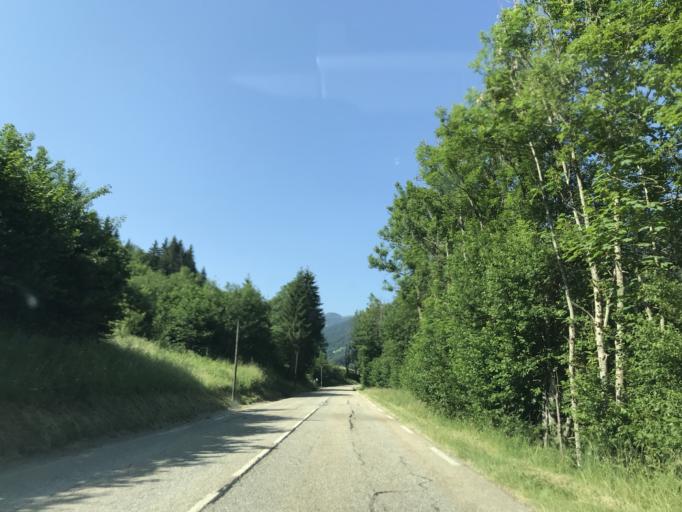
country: FR
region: Rhone-Alpes
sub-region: Departement de l'Isere
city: Allevard
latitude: 45.3251
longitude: 6.0898
